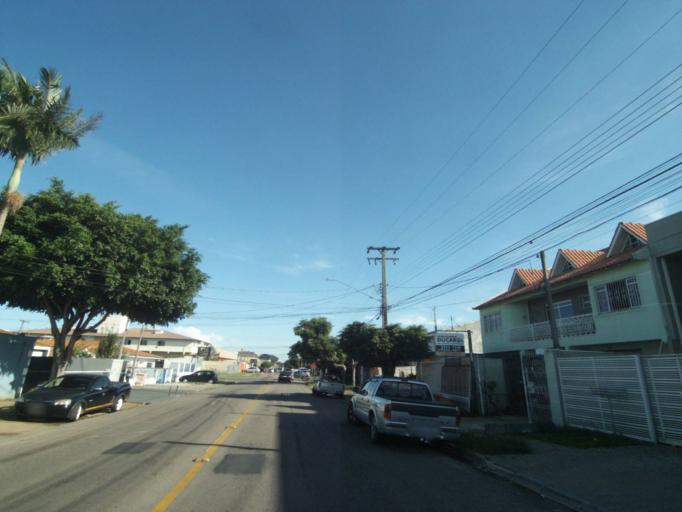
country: BR
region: Parana
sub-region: Pinhais
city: Pinhais
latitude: -25.4601
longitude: -49.2070
